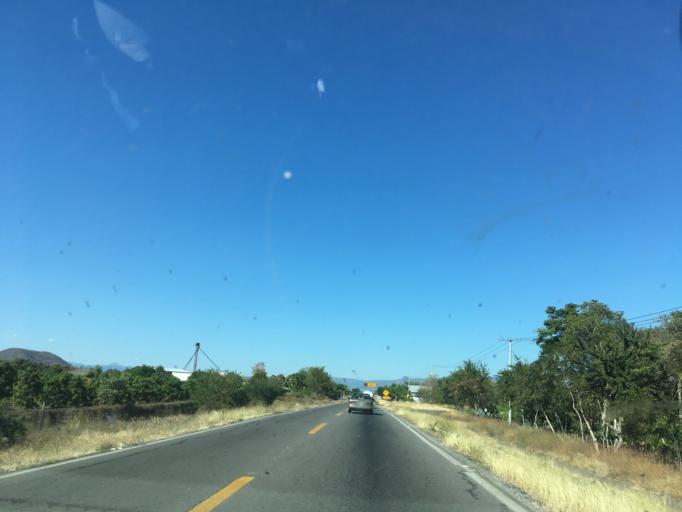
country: MX
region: Michoacan
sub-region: Gabriel Zamora
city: Lombardia
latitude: 19.0931
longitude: -102.0582
